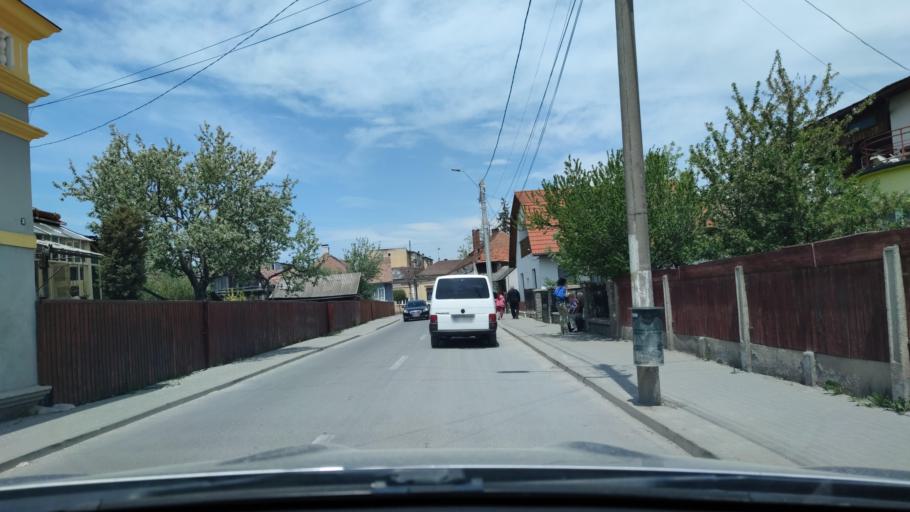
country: RO
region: Harghita
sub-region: Municipiul Gheorgheni
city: Gheorgheni
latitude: 46.7198
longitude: 25.5948
